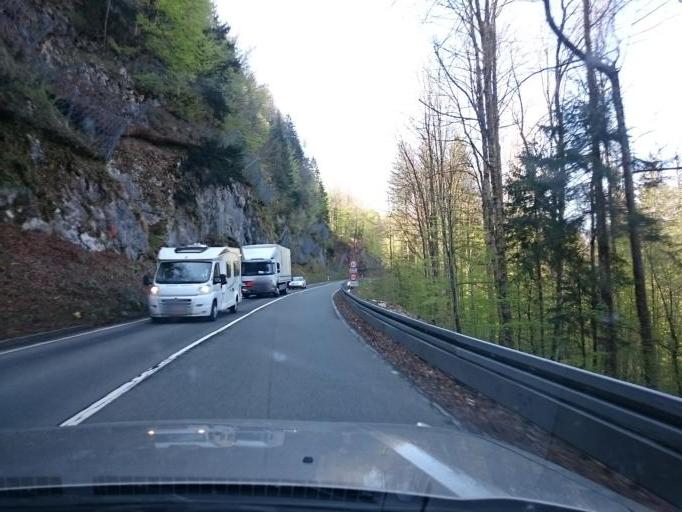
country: DE
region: Bavaria
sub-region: Upper Bavaria
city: Kochel
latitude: 47.6365
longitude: 11.3571
